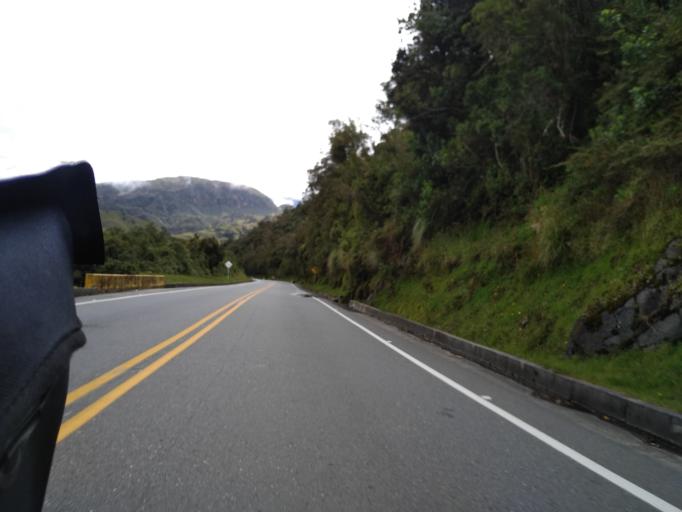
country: CO
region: Tolima
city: Herveo
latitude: 5.0262
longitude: -75.3344
